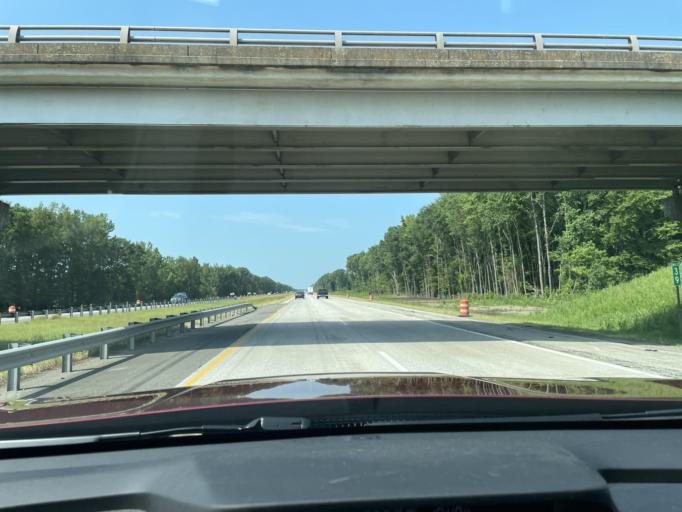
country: US
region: Arkansas
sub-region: White County
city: Searcy
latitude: 35.1718
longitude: -91.7688
